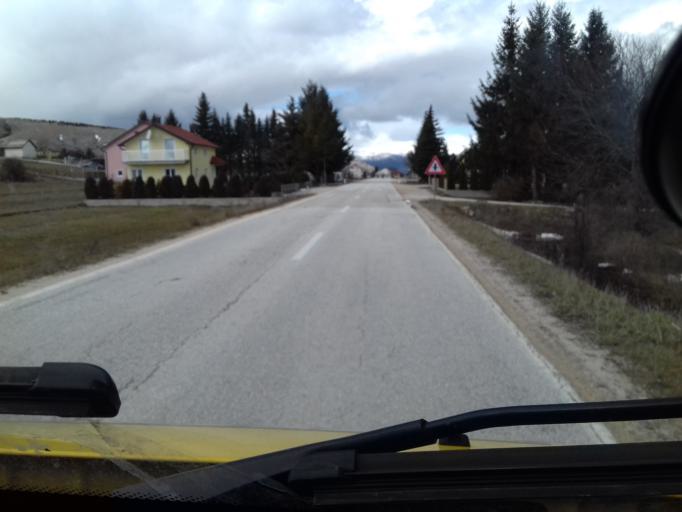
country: BA
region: Federation of Bosnia and Herzegovina
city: Tomislavgrad
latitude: 43.6284
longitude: 17.2495
